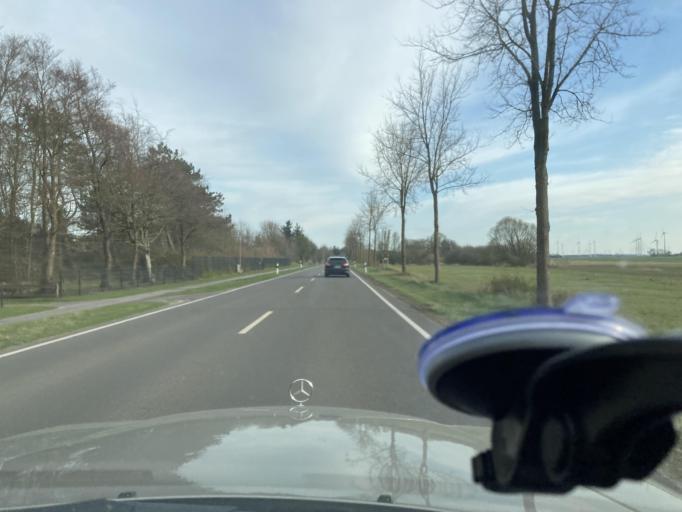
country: DE
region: Schleswig-Holstein
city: Stelle-Wittenwurth
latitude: 54.2916
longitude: 9.0417
